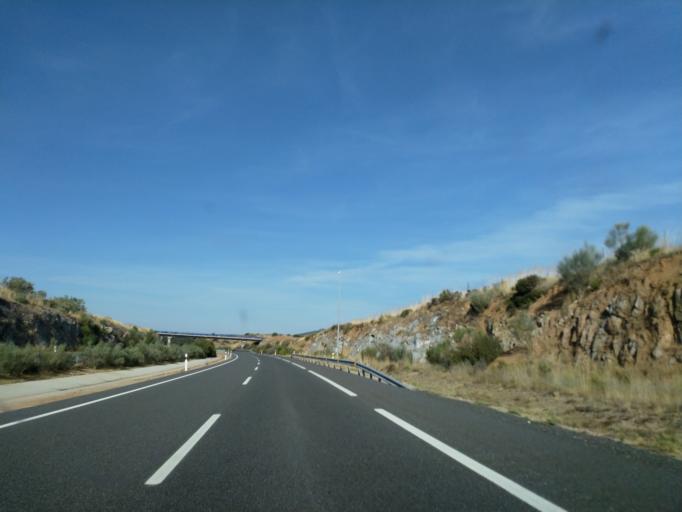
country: ES
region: Castille and Leon
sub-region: Provincia de Avila
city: Mediana de Voltoya
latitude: 40.7018
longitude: -4.5690
